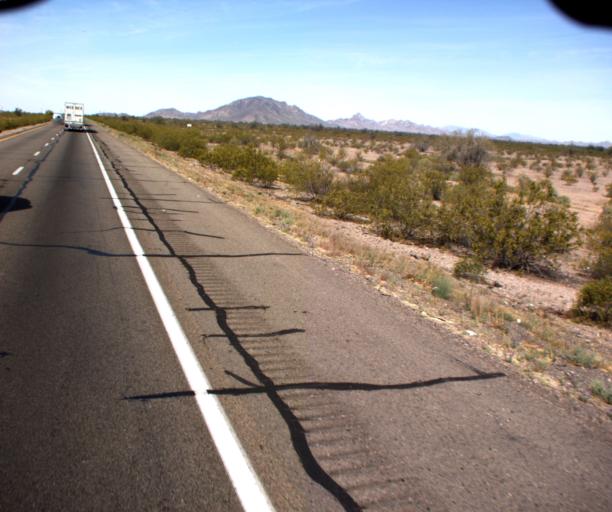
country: US
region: Arizona
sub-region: Maricopa County
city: Buckeye
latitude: 33.5058
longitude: -112.9807
